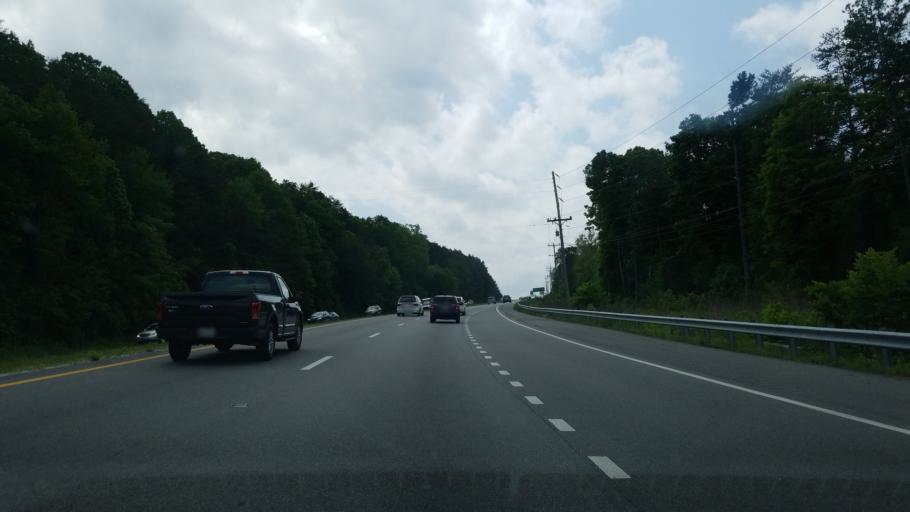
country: US
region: Tennessee
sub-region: Hamilton County
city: Falling Water
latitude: 35.1774
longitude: -85.2473
